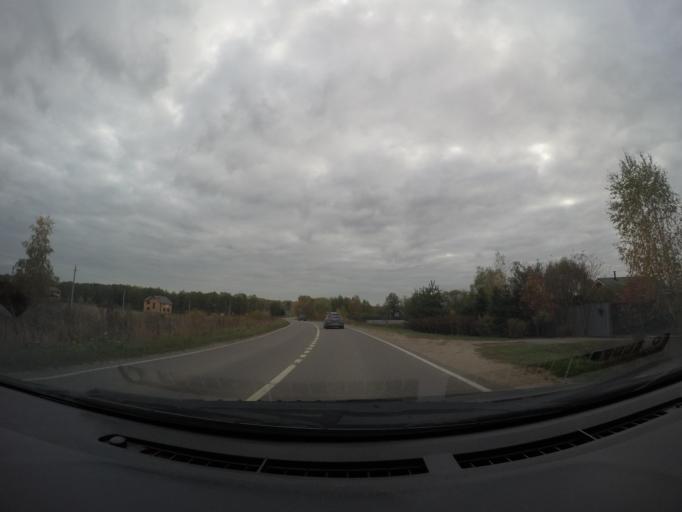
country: RU
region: Moskovskaya
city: Gzhel'
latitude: 55.6307
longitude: 38.4244
